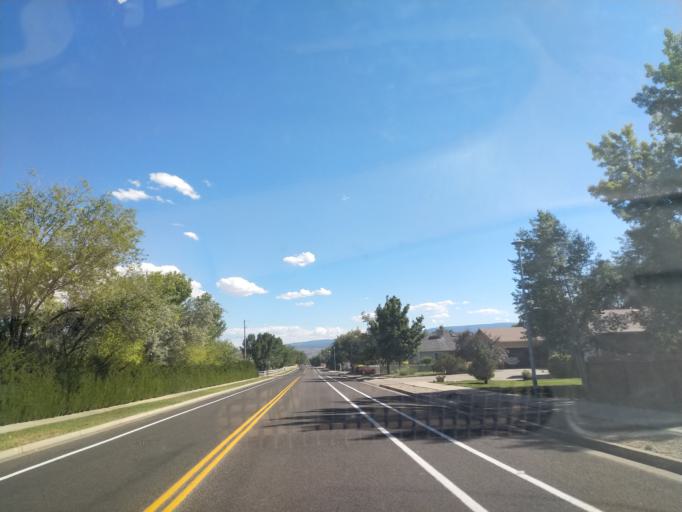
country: US
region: Colorado
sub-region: Mesa County
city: Grand Junction
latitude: 39.0910
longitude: -108.5478
